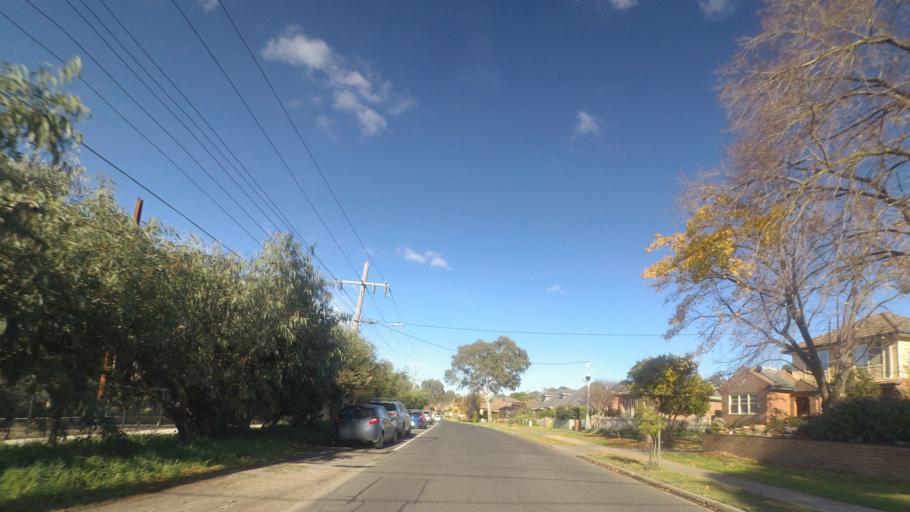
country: AU
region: Victoria
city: Macleod
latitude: -37.7360
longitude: 145.0654
